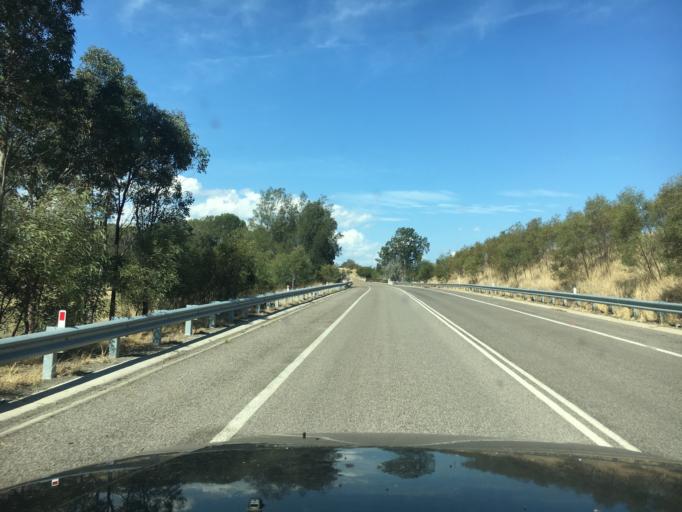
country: AU
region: New South Wales
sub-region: Cessnock
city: Branxton
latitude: -32.6554
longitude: 151.3265
